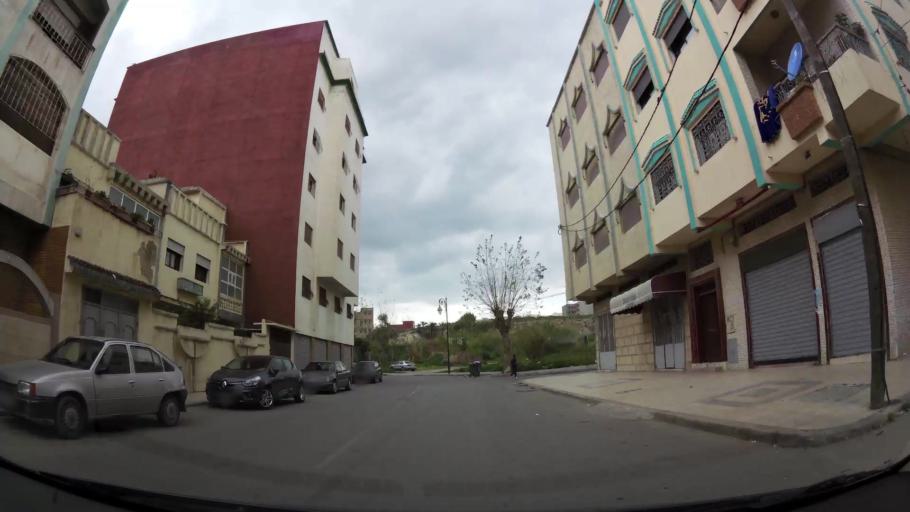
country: MA
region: Tanger-Tetouan
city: Tetouan
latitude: 35.5659
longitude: -5.3608
